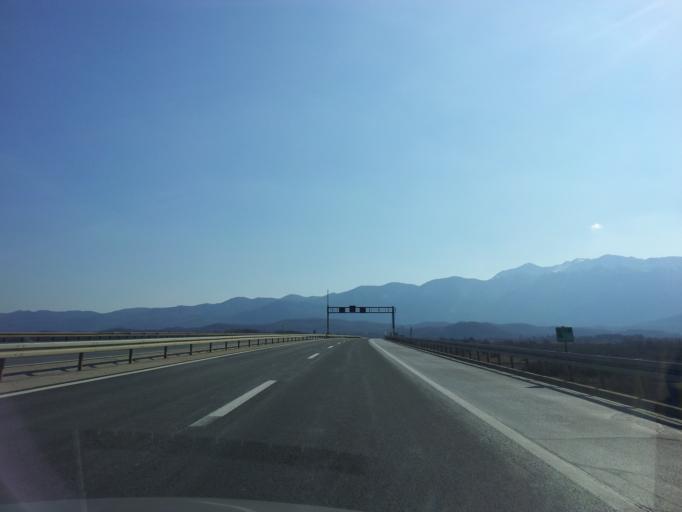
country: HR
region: Zadarska
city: Obrovac
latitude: 44.4023
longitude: 15.6369
